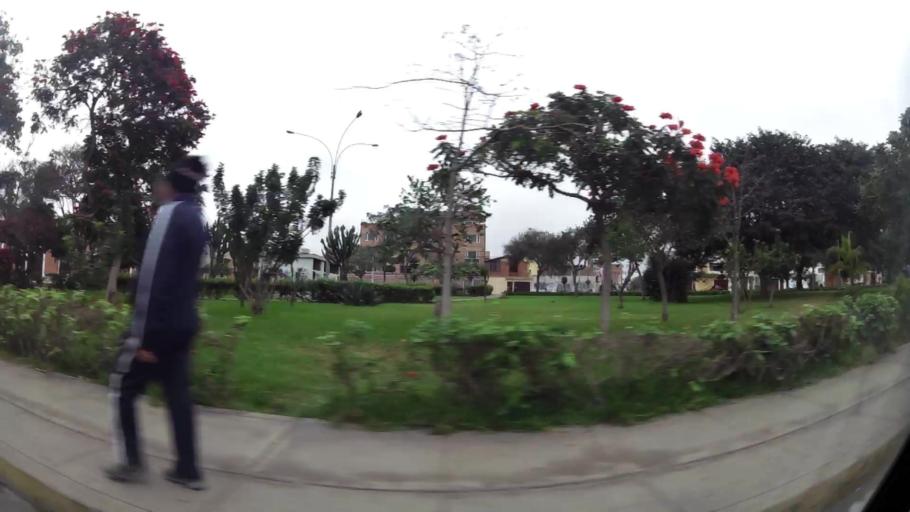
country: PE
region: Callao
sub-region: Callao
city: Callao
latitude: -12.0633
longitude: -77.0745
